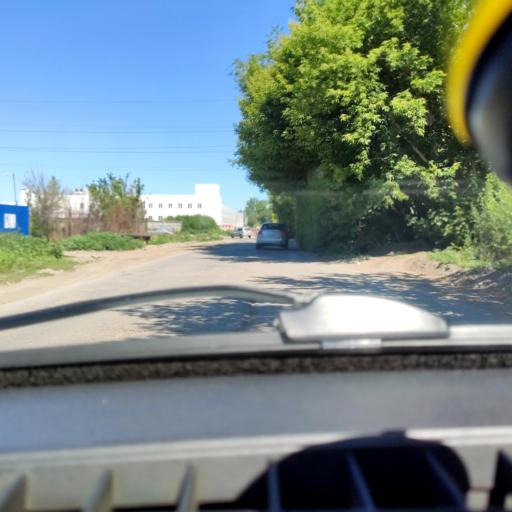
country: RU
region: Samara
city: Tol'yatti
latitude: 53.5689
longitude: 49.2946
